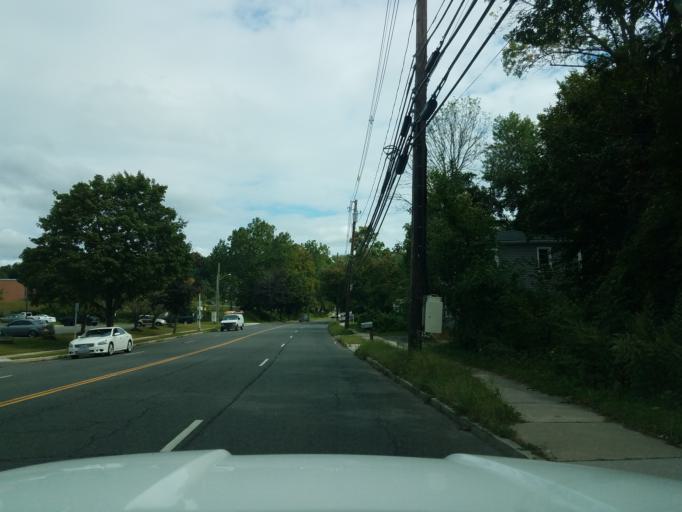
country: US
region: Connecticut
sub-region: Fairfield County
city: Danbury
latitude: 41.4130
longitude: -73.4535
